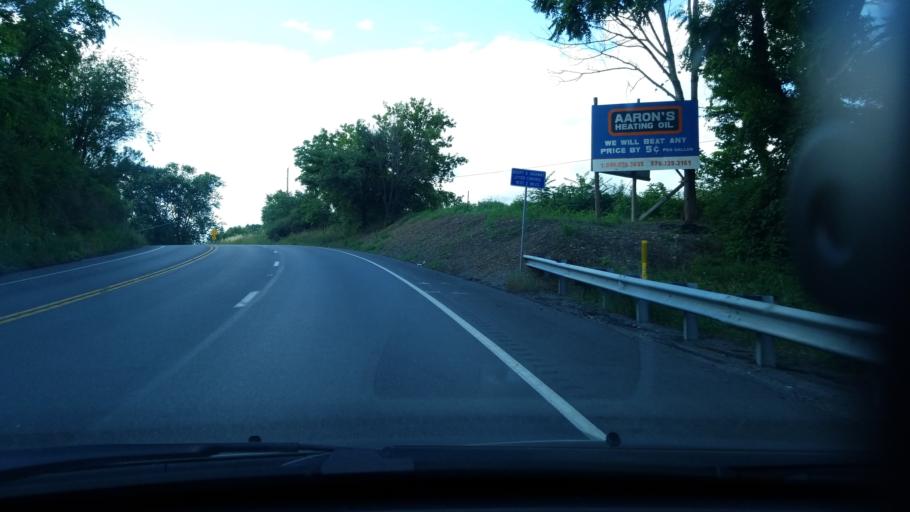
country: US
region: Pennsylvania
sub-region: Northumberland County
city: Elysburg
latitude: 40.8819
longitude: -76.5503
